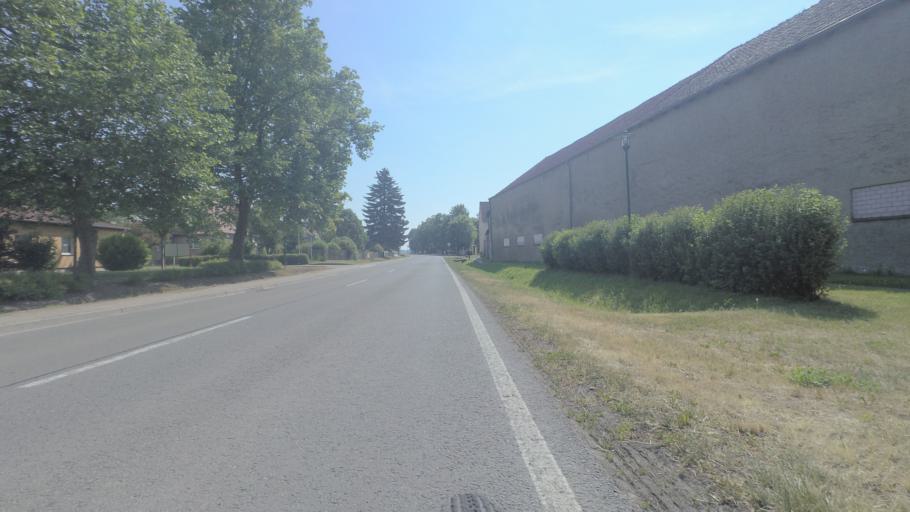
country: DE
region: Saxony-Anhalt
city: Nachterstedt
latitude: 51.8361
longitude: 11.3296
